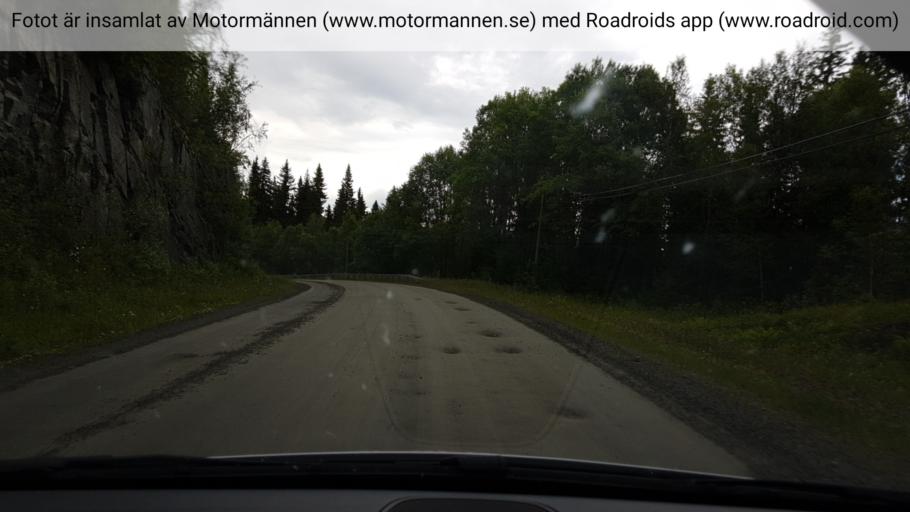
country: SE
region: Jaemtland
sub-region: Are Kommun
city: Are
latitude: 63.6817
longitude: 12.9013
